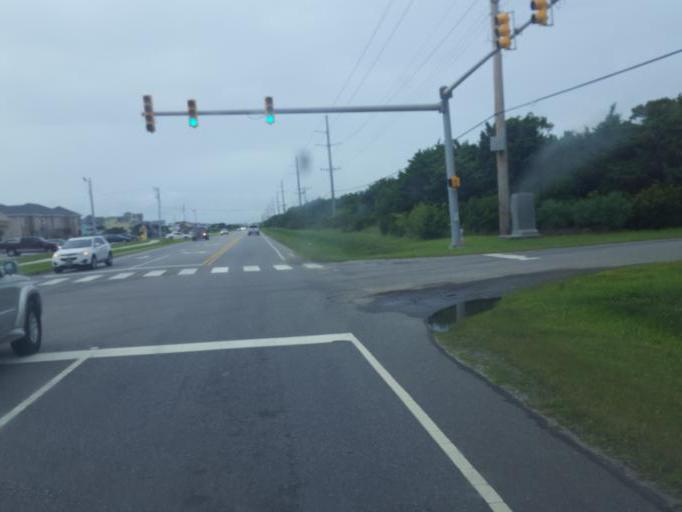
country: US
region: North Carolina
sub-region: Dare County
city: Buxton
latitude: 35.3336
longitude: -75.5068
